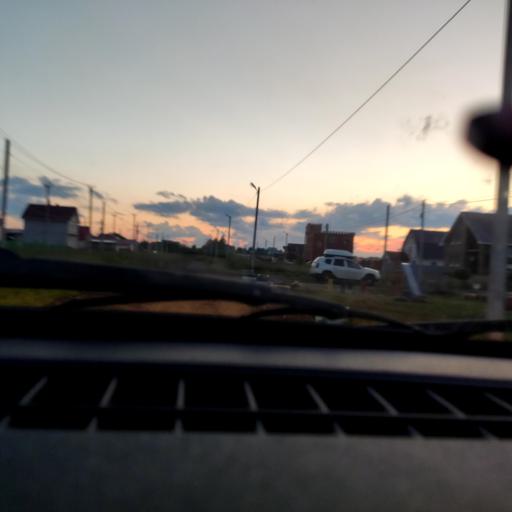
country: RU
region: Bashkortostan
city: Kabakovo
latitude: 54.6099
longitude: 56.1043
